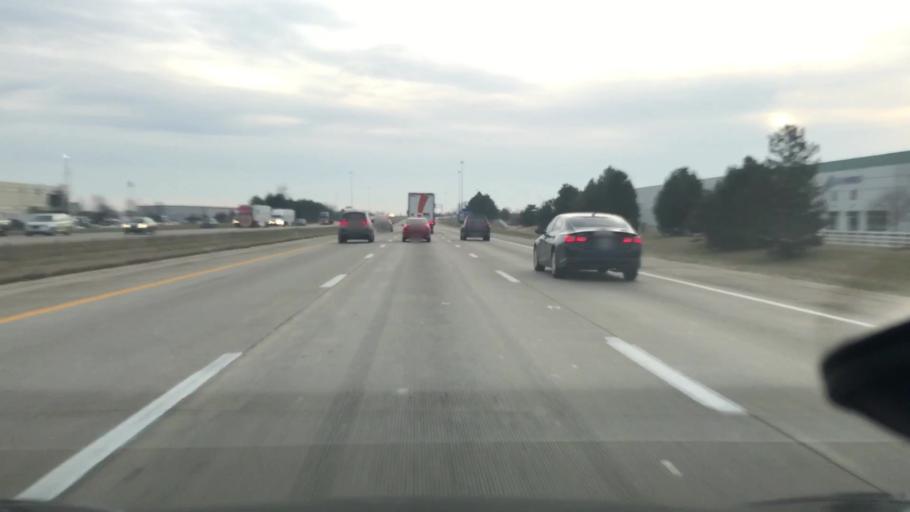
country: US
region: Ohio
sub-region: Franklin County
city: Grove City
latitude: 39.9061
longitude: -83.0880
